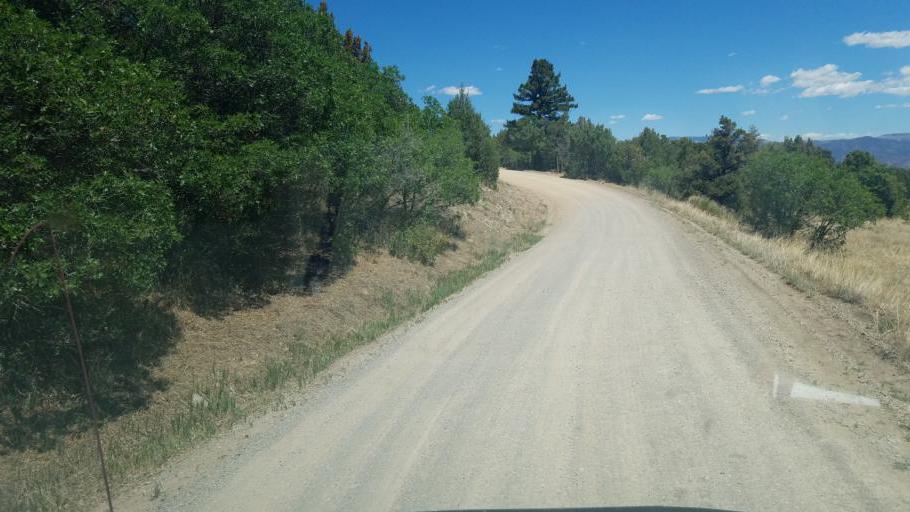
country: US
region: Colorado
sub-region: Custer County
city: Westcliffe
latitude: 38.3021
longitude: -105.6701
